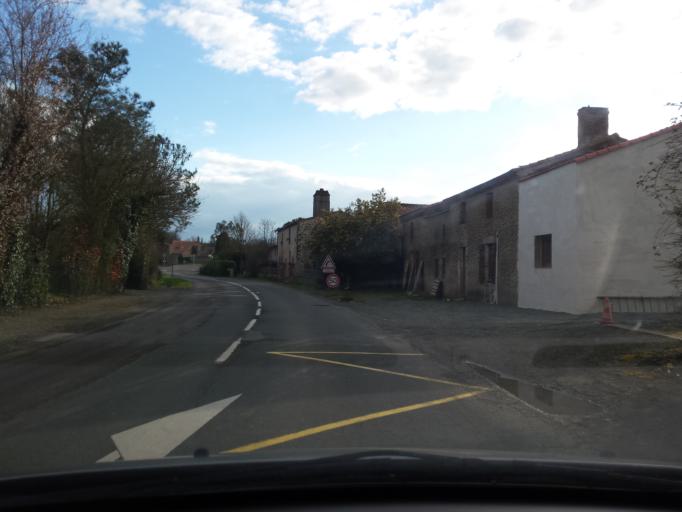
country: FR
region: Pays de la Loire
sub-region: Departement de la Vendee
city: Saint-Martin-des-Noyers
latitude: 46.7149
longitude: -1.2107
